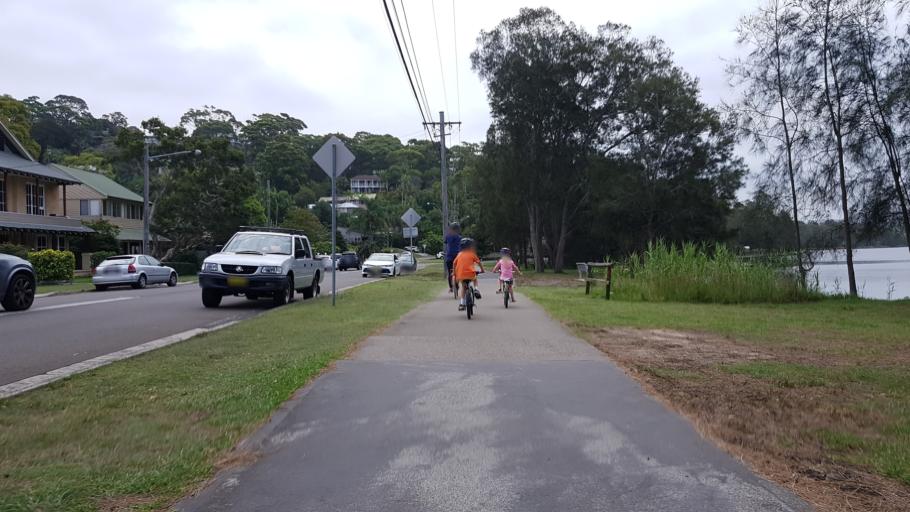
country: AU
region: New South Wales
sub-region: Warringah
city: Narrabeen
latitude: -33.7215
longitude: 151.2935
